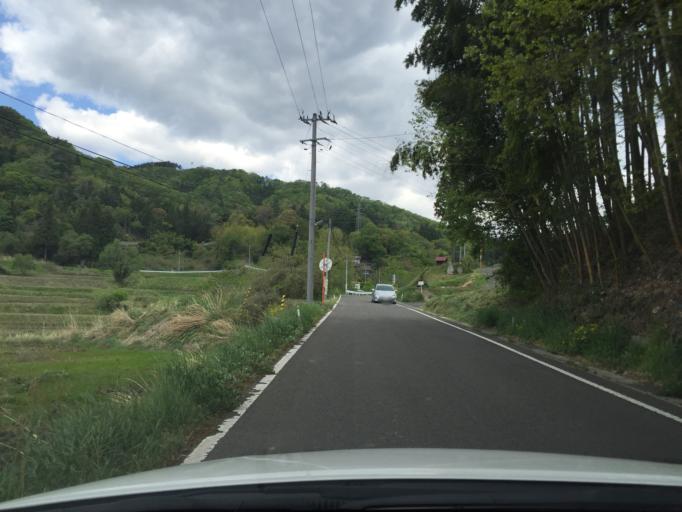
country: JP
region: Fukushima
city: Fukushima-shi
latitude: 37.7031
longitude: 140.5566
